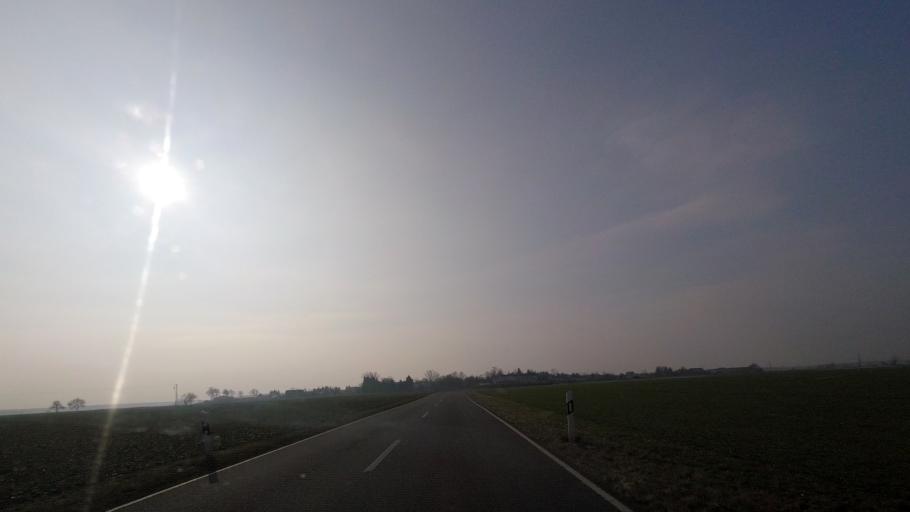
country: DE
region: Brandenburg
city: Juterbog
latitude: 51.8992
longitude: 13.0723
